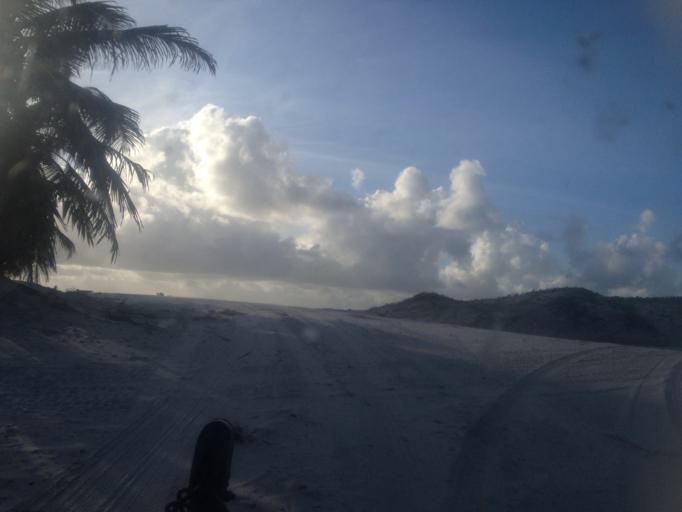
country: BR
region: Sergipe
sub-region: Indiaroba
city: Indiaroba
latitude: -11.4673
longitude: -37.3556
